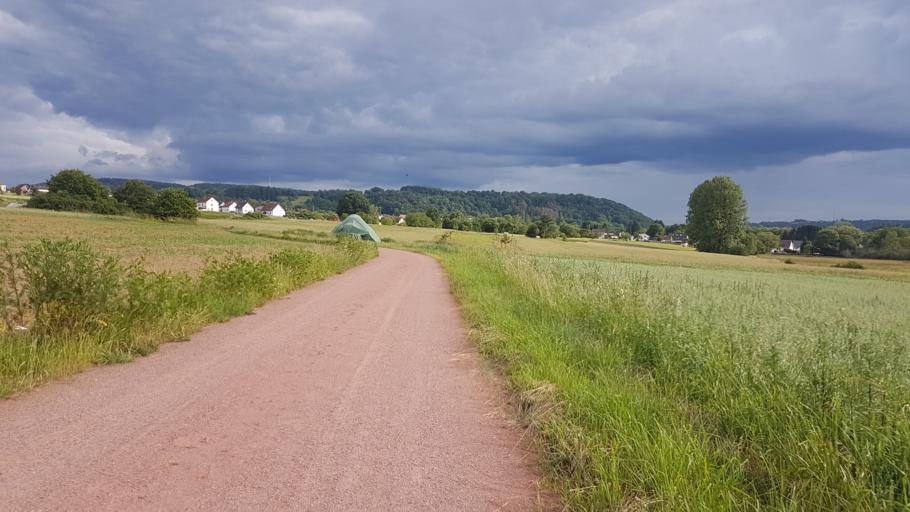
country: DE
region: Saarland
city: Britten
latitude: 49.4877
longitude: 6.7024
